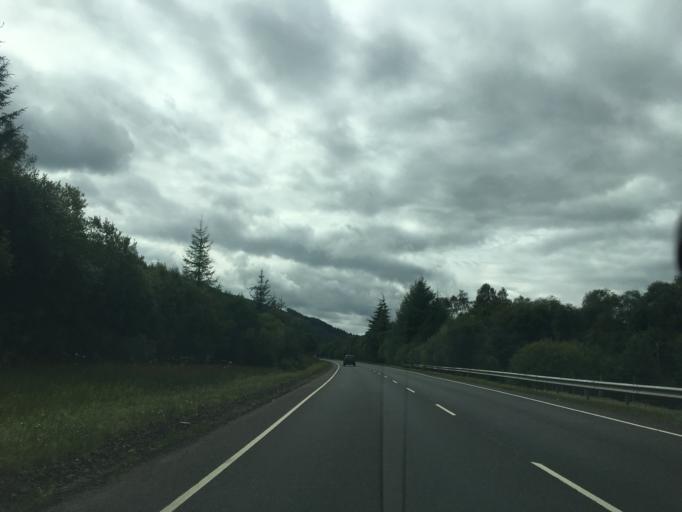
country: GB
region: Scotland
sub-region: Stirling
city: Callander
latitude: 56.3697
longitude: -4.2969
